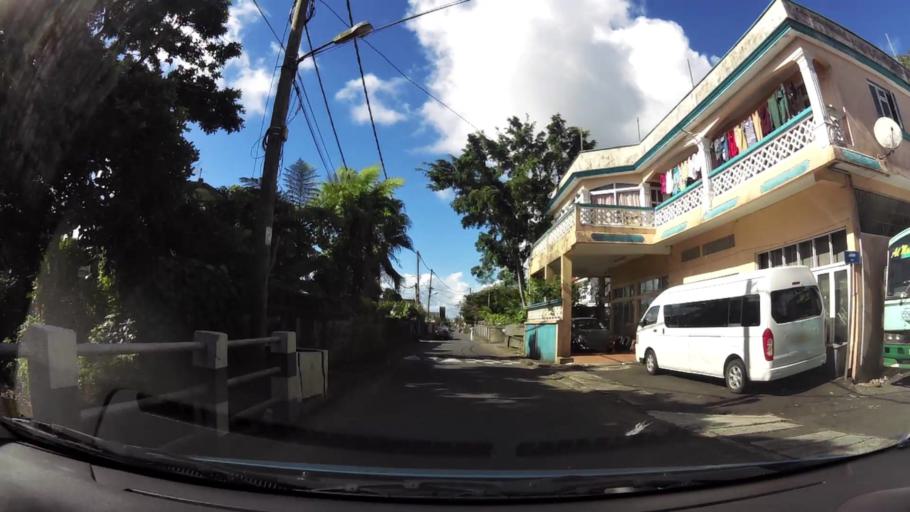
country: MU
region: Plaines Wilhems
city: Curepipe
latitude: -20.3252
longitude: 57.5318
